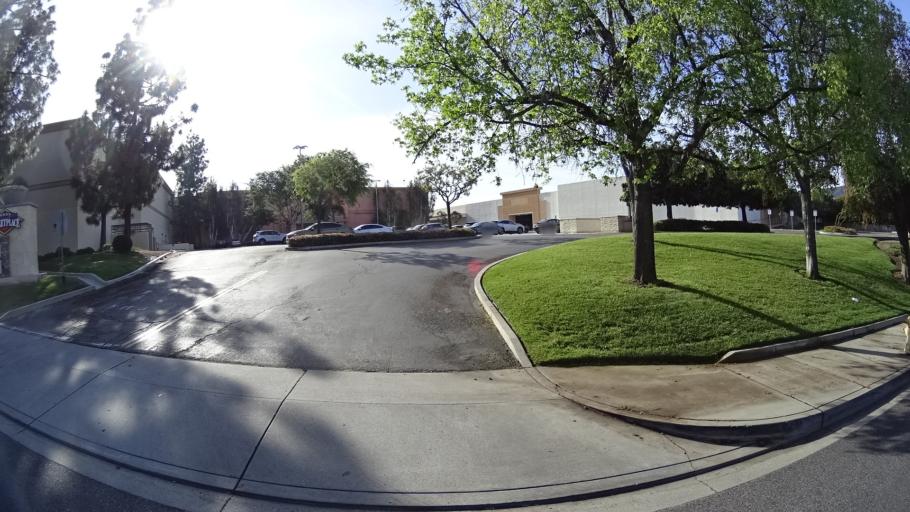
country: US
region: California
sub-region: Ventura County
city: Thousand Oaks
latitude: 34.1825
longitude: -118.8802
